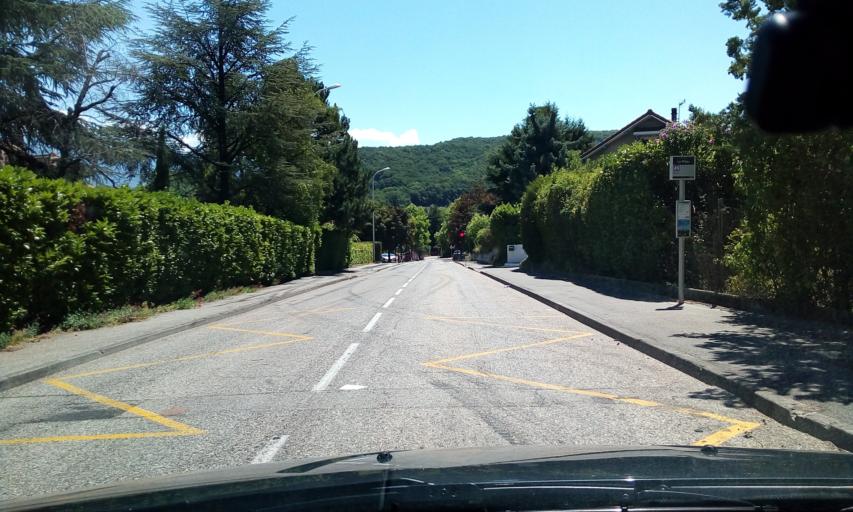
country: FR
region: Rhone-Alpes
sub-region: Departement de l'Isere
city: Seyssins
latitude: 45.1570
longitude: 5.6787
